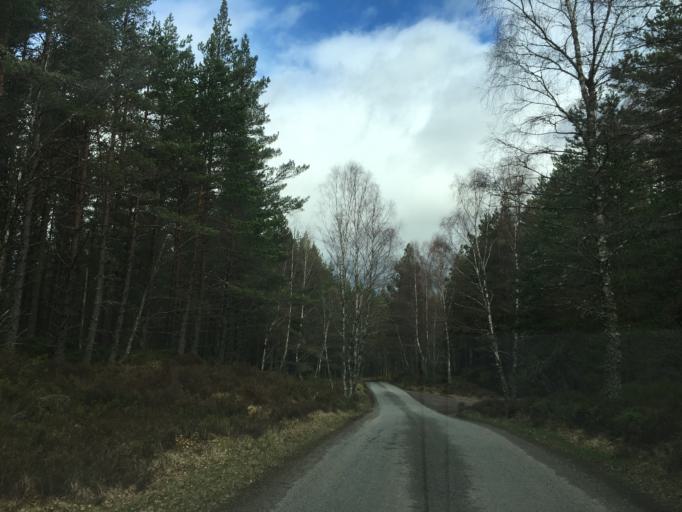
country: GB
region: Scotland
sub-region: Highland
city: Kingussie
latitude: 57.1025
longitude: -3.9218
